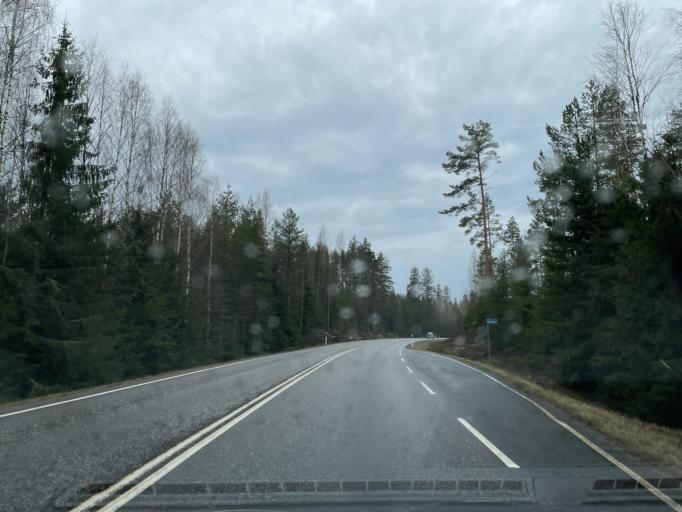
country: FI
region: Paijanne Tavastia
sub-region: Lahti
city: Auttoinen
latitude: 61.2347
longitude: 25.1111
